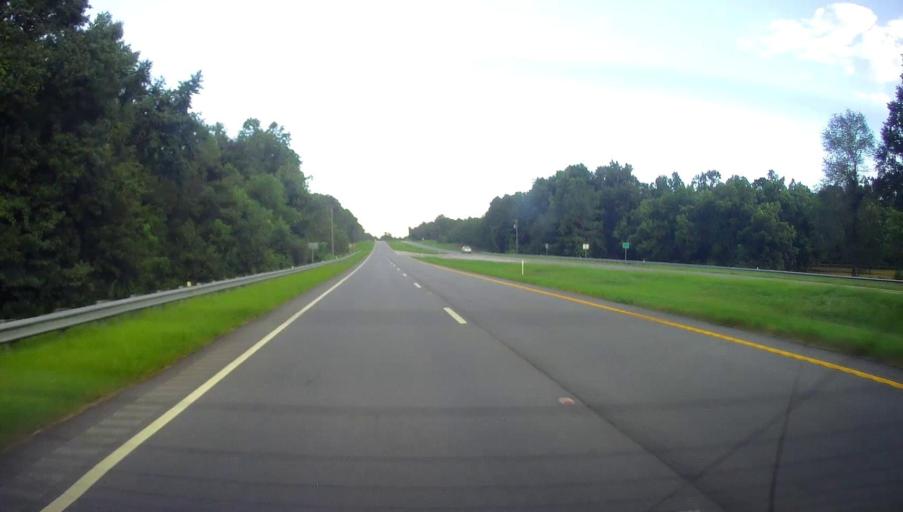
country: US
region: Georgia
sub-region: Pulaski County
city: Hawkinsville
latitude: 32.3451
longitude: -83.5729
